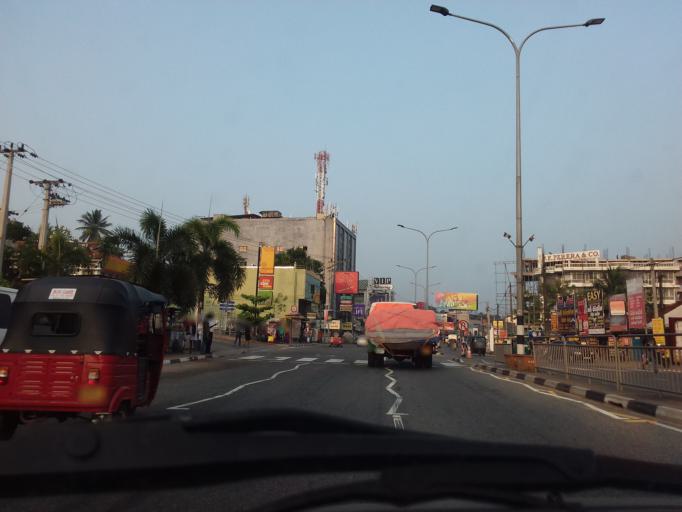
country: LK
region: Western
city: Kelaniya
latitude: 6.9719
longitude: 79.9168
